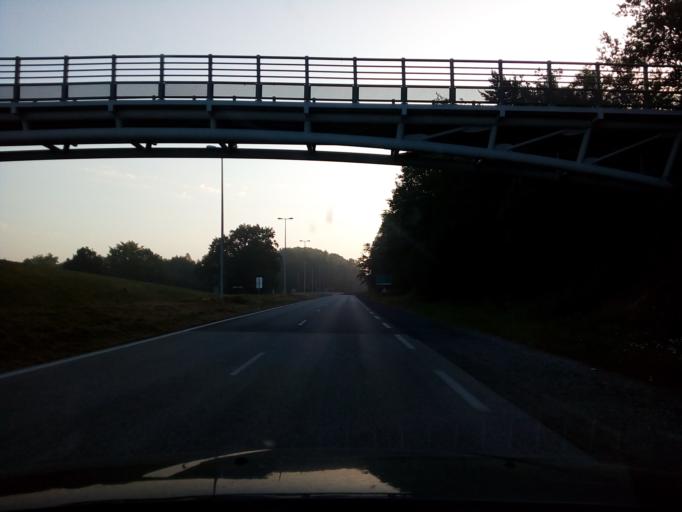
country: FR
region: Limousin
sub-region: Departement de la Haute-Vienne
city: Couzeix
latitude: 45.8664
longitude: 1.2769
